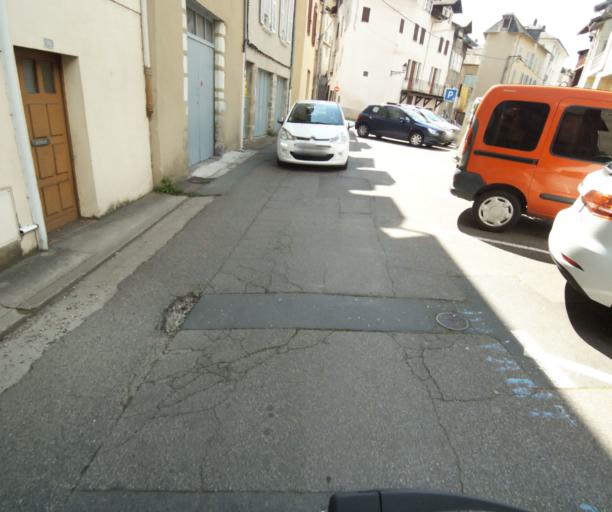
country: FR
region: Limousin
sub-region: Departement de la Correze
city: Tulle
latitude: 45.2700
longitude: 1.7699
